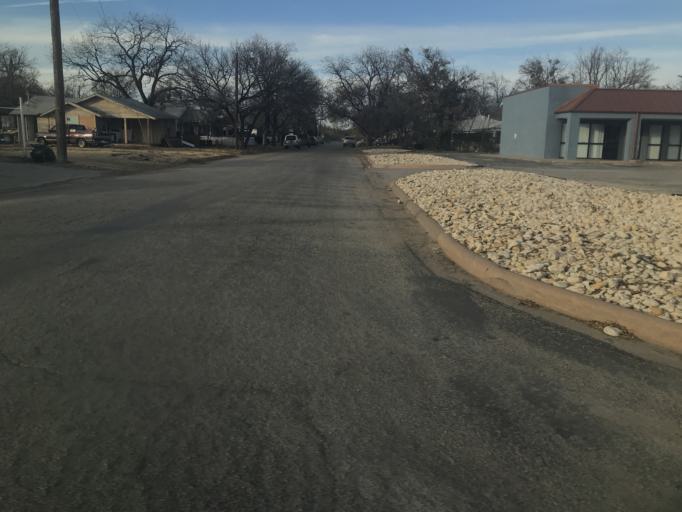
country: US
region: Texas
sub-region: Taylor County
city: Abilene
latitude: 32.4322
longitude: -99.7397
